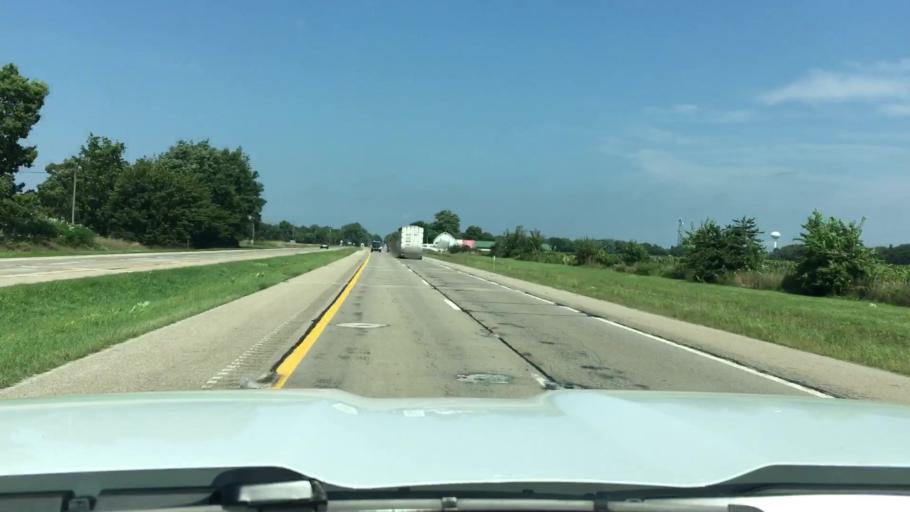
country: US
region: Michigan
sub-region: Kalamazoo County
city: Schoolcraft
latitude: 42.1005
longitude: -85.6368
